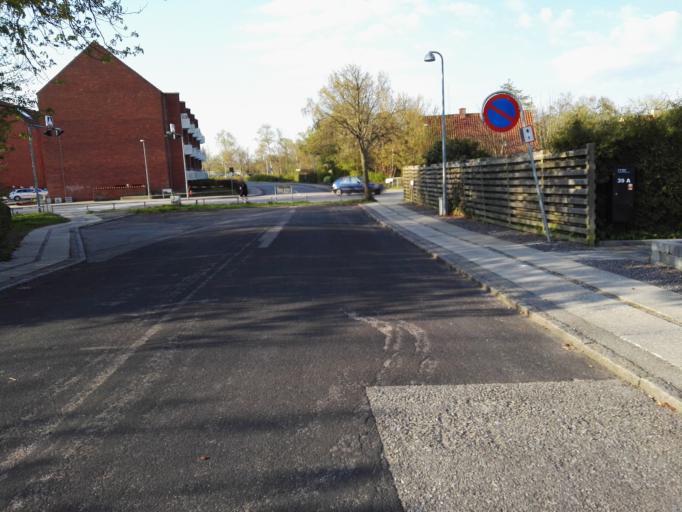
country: DK
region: Capital Region
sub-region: Ballerup Kommune
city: Ballerup
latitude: 55.7334
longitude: 12.3546
